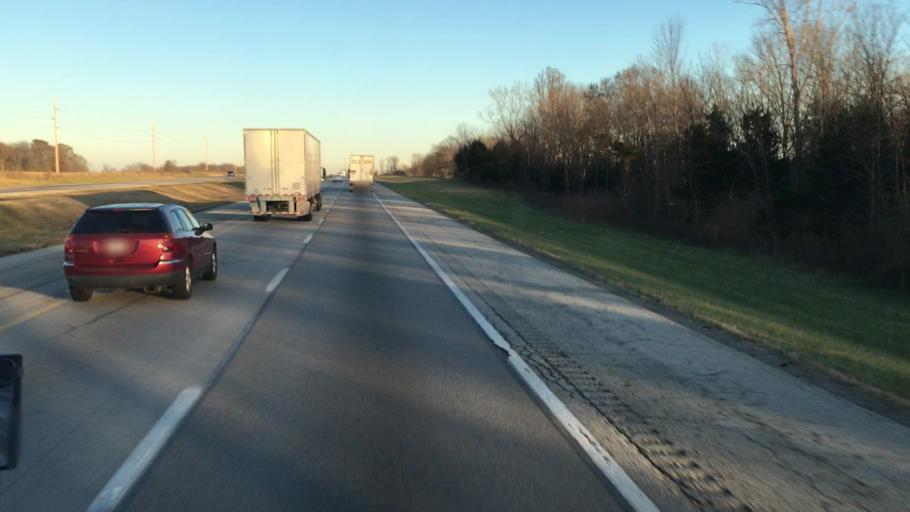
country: US
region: Ohio
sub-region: Preble County
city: Lewisburg
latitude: 39.8360
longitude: -84.5779
